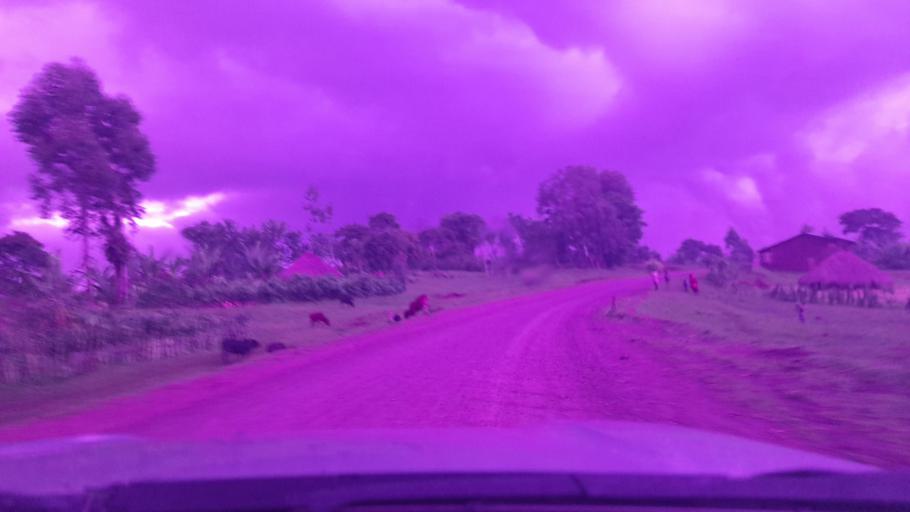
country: ET
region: Southern Nations, Nationalities, and People's Region
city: Mizan Teferi
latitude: 6.9026
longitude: 35.8392
